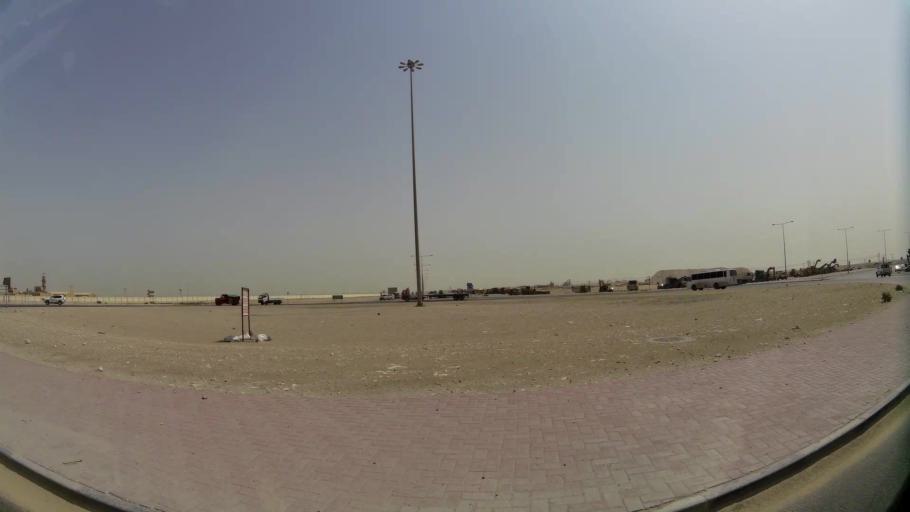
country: QA
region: Baladiyat ar Rayyan
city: Ar Rayyan
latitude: 25.1786
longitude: 51.3976
